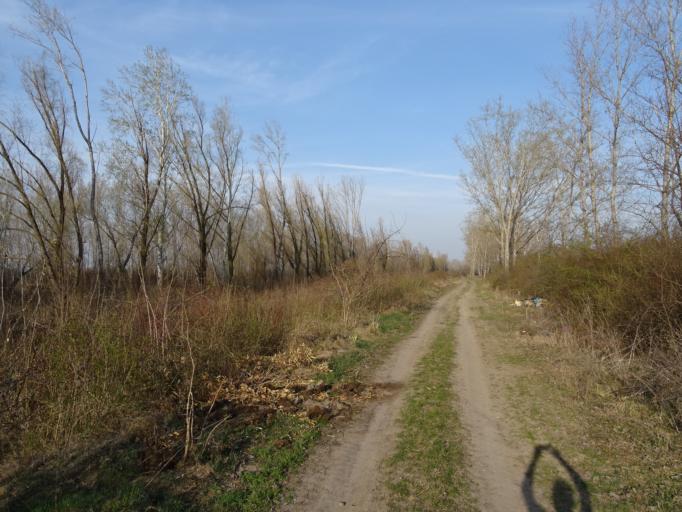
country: HU
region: Bacs-Kiskun
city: Tass
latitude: 47.0278
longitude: 19.0129
